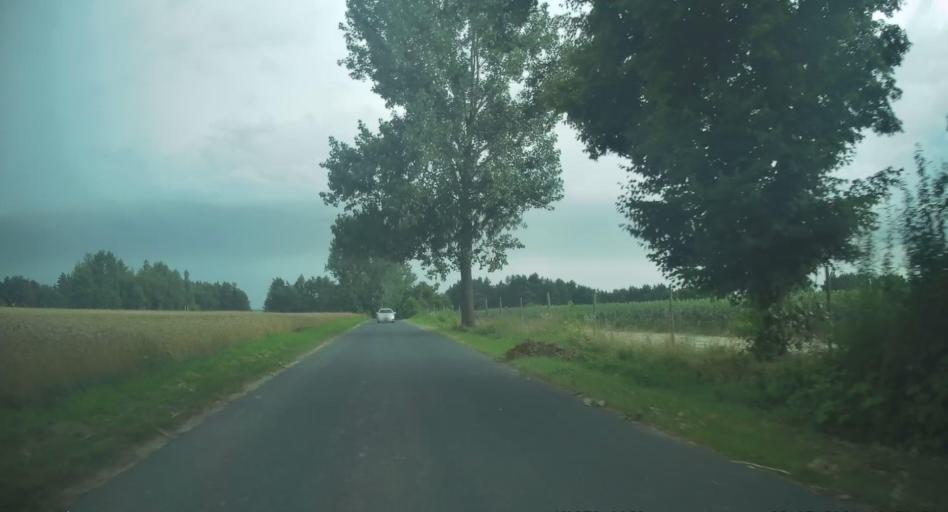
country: PL
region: Lodz Voivodeship
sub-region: Powiat rawski
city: Rawa Mazowiecka
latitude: 51.7627
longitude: 20.1858
